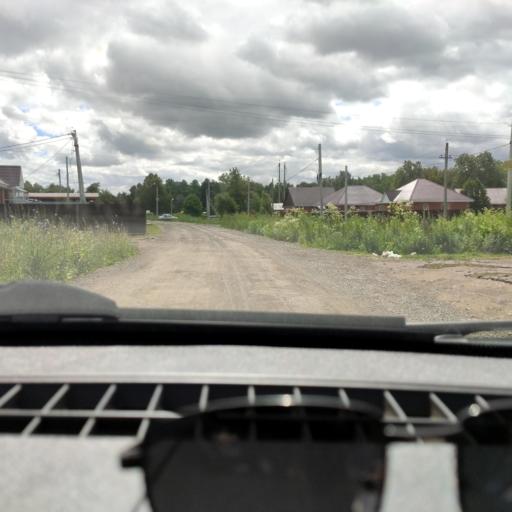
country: RU
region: Bashkortostan
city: Ufa
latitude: 54.6737
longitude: 56.0934
